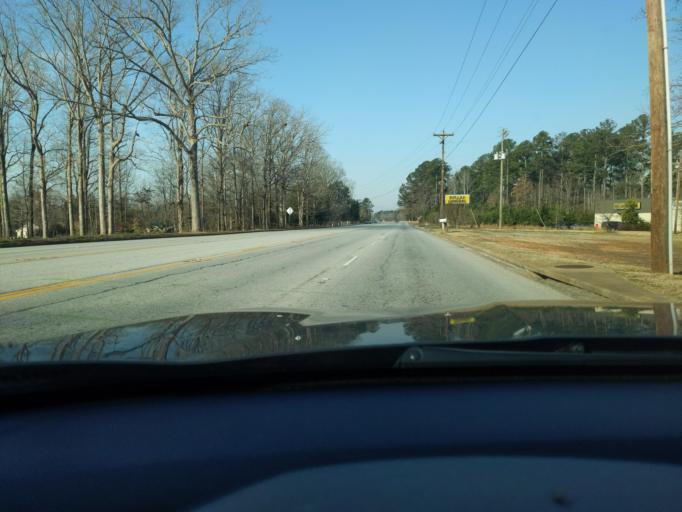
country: US
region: South Carolina
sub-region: Greenwood County
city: Greenwood
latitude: 34.1902
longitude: -82.2265
